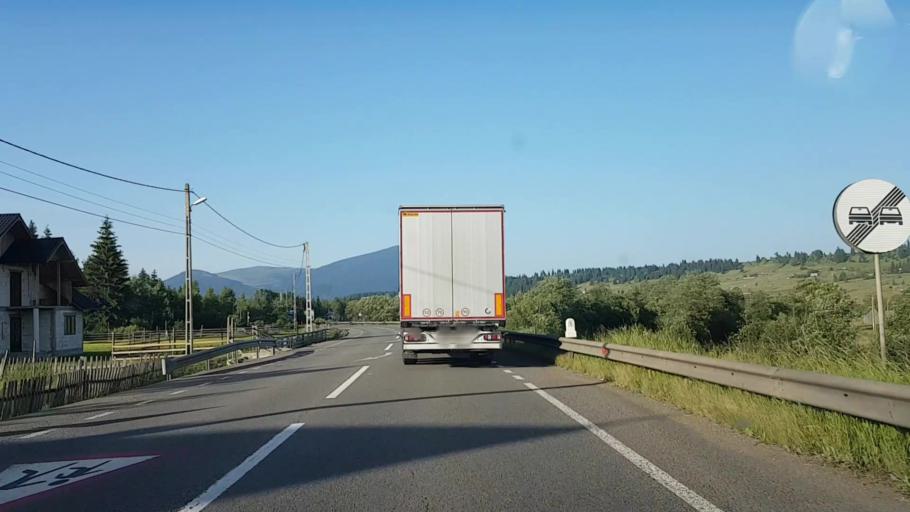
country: RO
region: Suceava
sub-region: Comuna Poiana Stampei
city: Poiana Stampei
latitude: 47.3343
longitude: 25.1615
